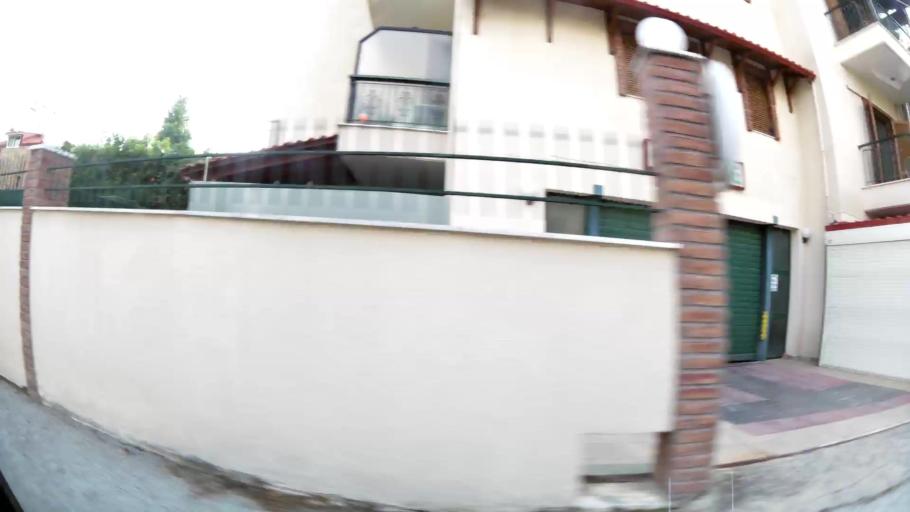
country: GR
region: Central Macedonia
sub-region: Nomos Thessalonikis
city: Oraiokastro
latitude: 40.7182
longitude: 22.9035
